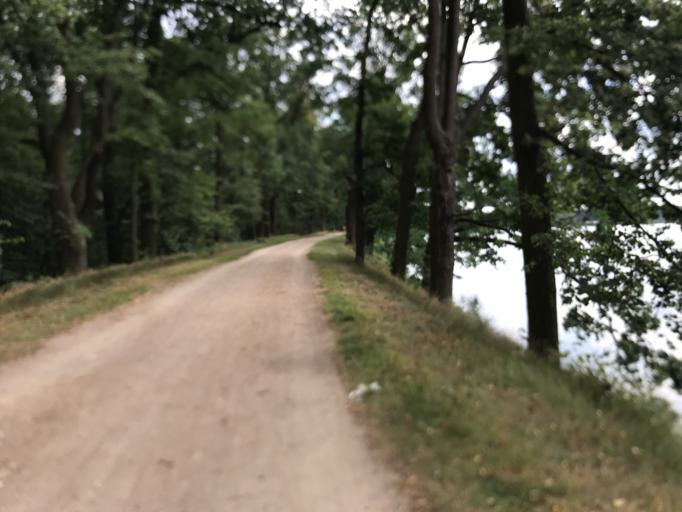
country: CZ
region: Jihocesky
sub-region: Okres Jindrichuv Hradec
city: Trebon
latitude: 48.9926
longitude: 14.7727
